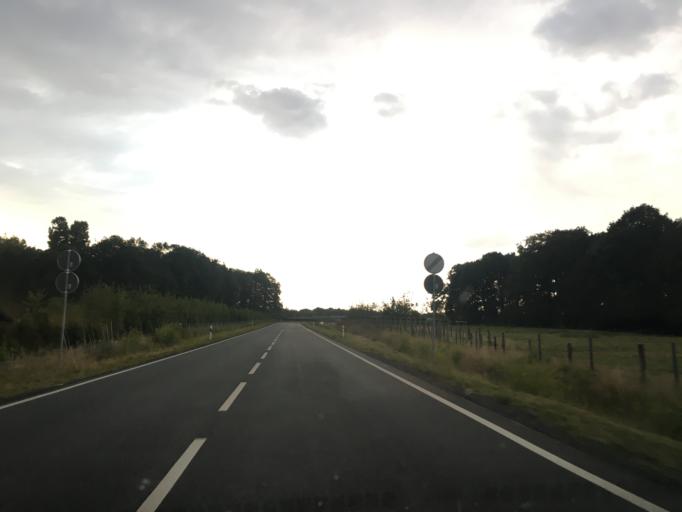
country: DE
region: North Rhine-Westphalia
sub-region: Regierungsbezirk Munster
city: Telgte
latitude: 51.9225
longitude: 7.7134
